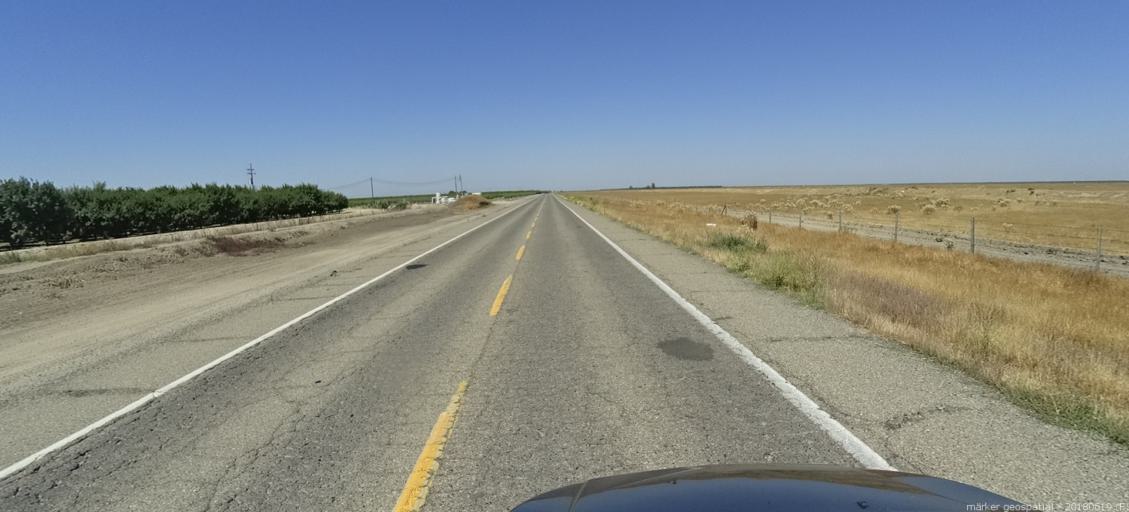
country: US
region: California
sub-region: Fresno County
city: Mendota
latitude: 36.8510
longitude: -120.2262
